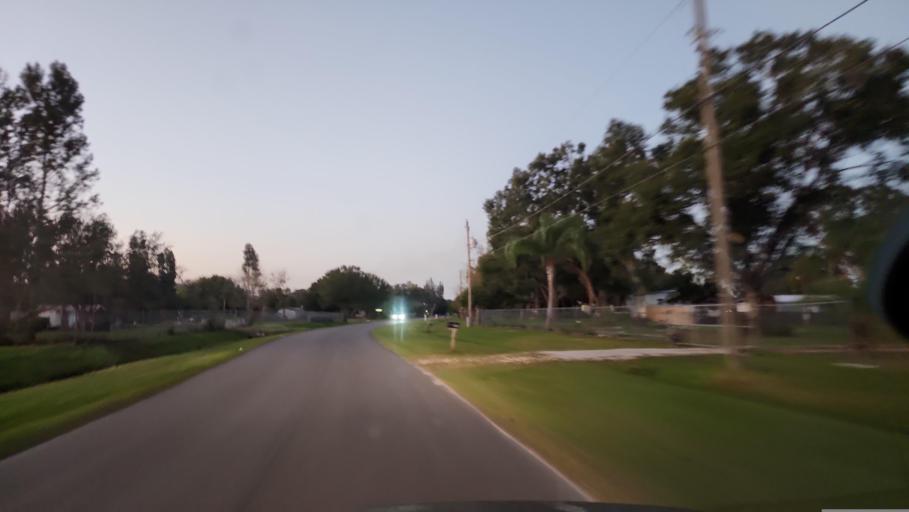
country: US
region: Florida
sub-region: Hillsborough County
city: Balm
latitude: 27.8019
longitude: -82.2745
